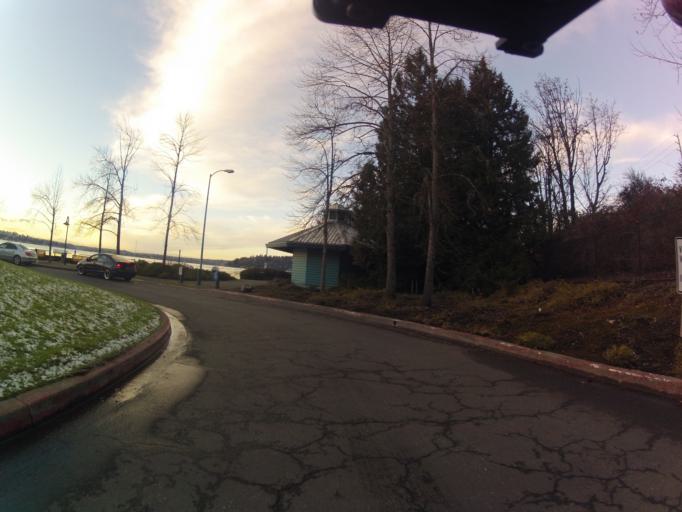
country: US
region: Washington
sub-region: King County
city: Renton
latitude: 47.5094
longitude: -122.2025
